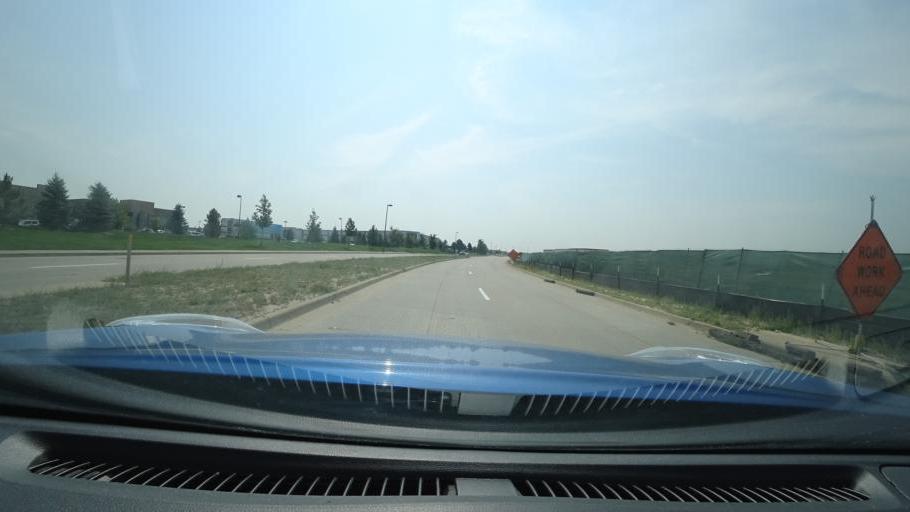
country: US
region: Colorado
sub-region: Adams County
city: Aurora
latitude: 39.7723
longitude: -104.7793
